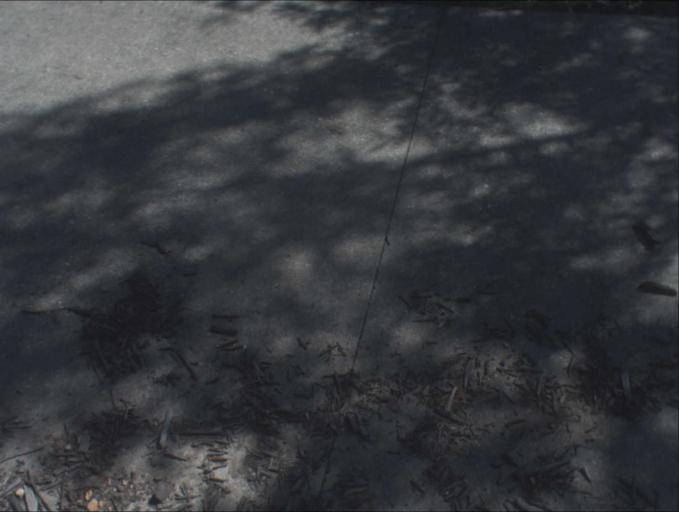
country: AU
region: Queensland
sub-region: Logan
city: Waterford West
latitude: -27.7150
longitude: 153.1527
